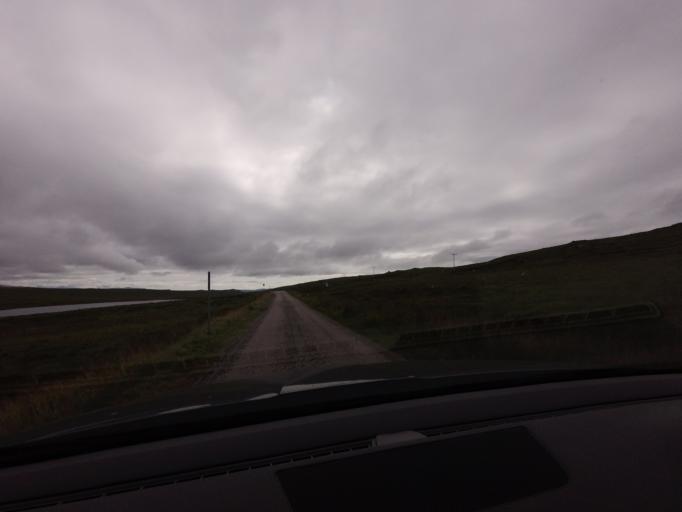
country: GB
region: Scotland
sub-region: Highland
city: Ullapool
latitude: 58.4572
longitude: -4.9238
